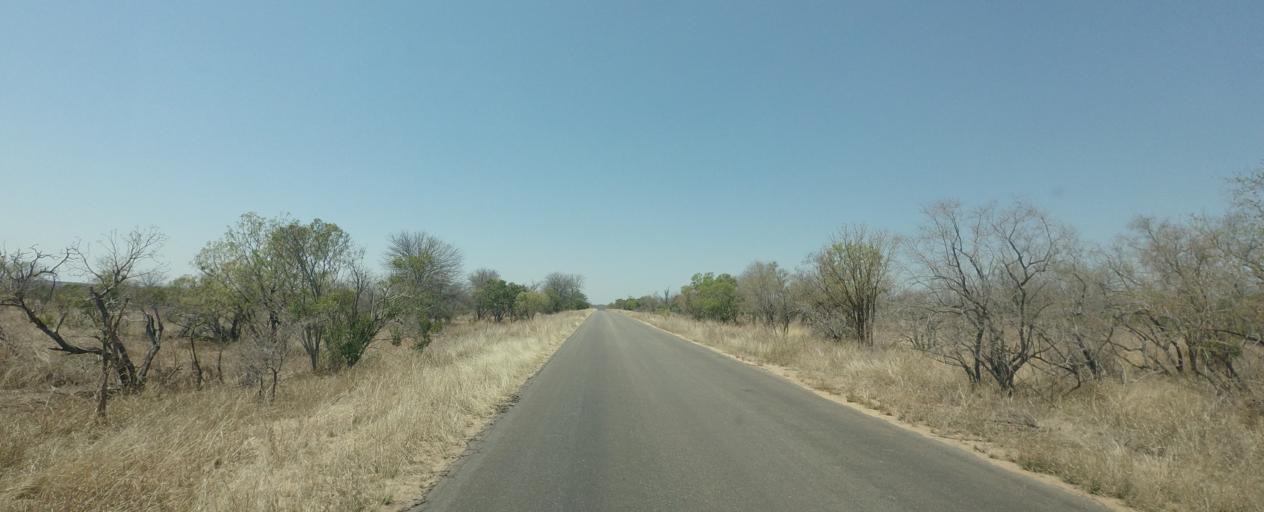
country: ZA
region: Limpopo
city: Thulamahashi
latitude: -24.4716
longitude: 31.4296
